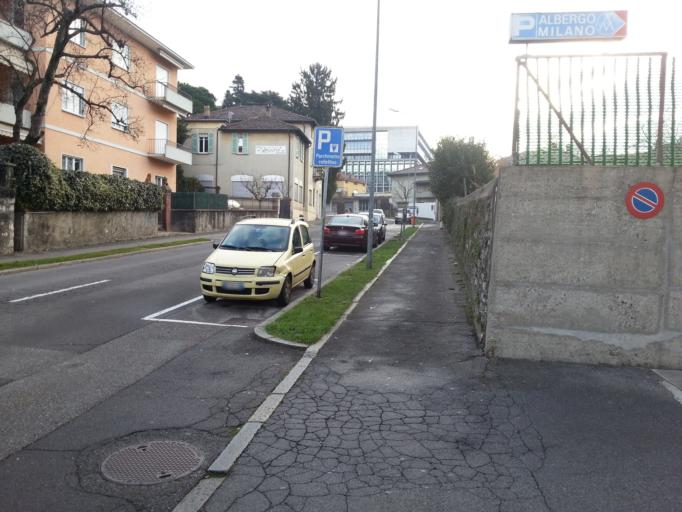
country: CH
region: Ticino
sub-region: Mendrisio District
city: Mendrisio
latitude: 45.8685
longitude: 8.9796
